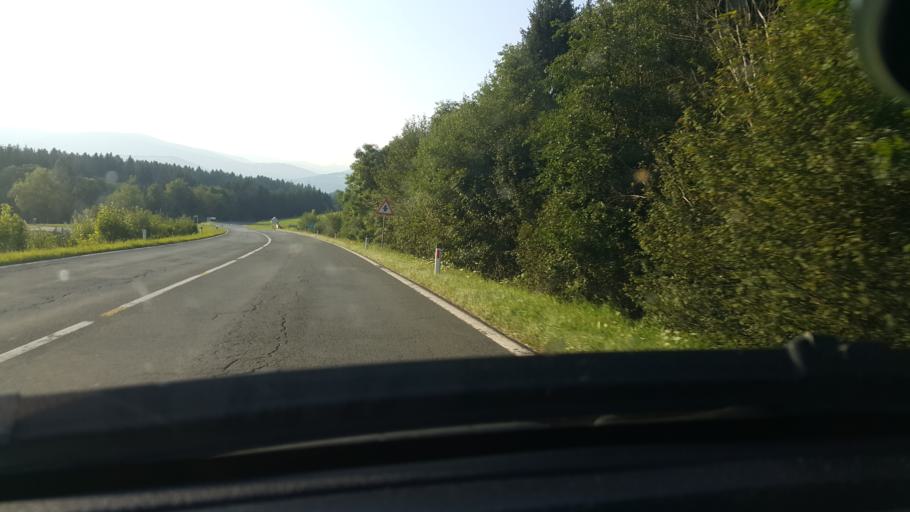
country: AT
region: Carinthia
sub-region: Politischer Bezirk Feldkirchen
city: Feldkirchen in Karnten
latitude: 46.6981
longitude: 14.1222
